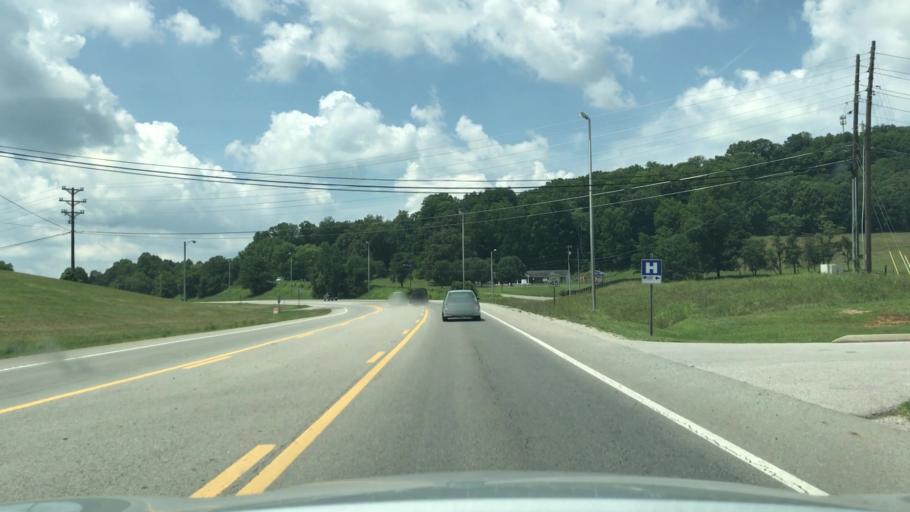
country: US
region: Tennessee
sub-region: Overton County
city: Livingston
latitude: 36.3942
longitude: -85.3295
